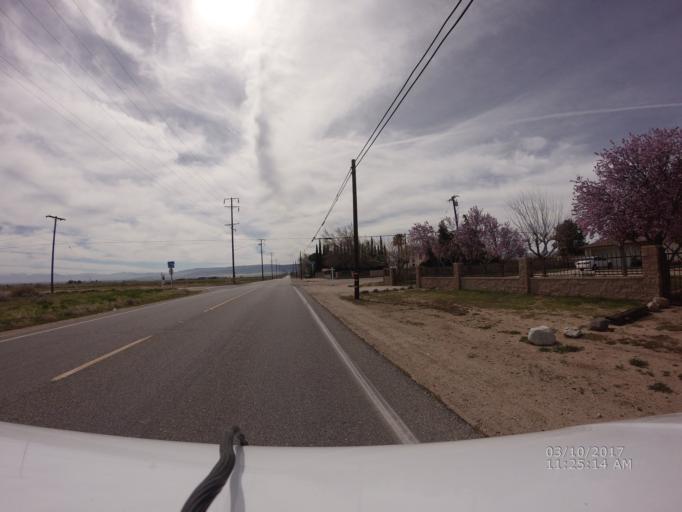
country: US
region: California
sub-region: Los Angeles County
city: Quartz Hill
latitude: 34.7477
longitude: -118.2899
